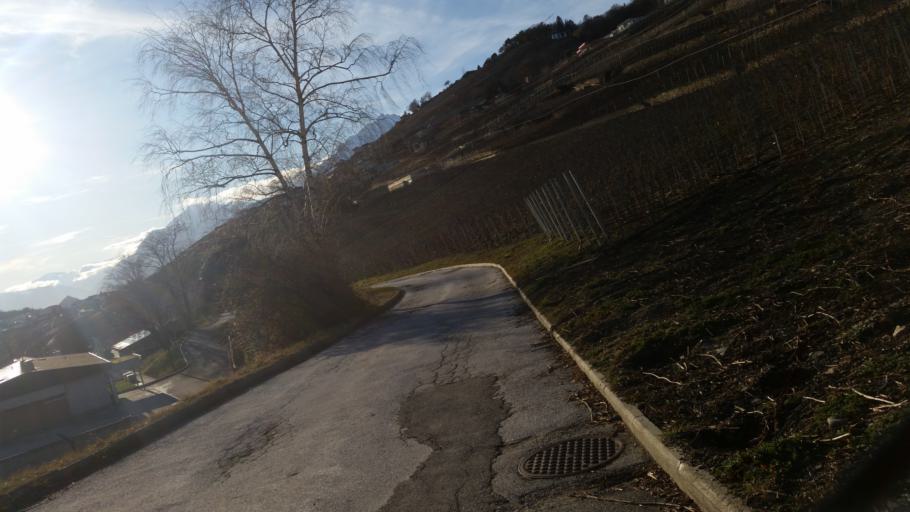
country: CH
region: Valais
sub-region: Sion District
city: Grimisuat
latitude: 46.2530
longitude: 7.3894
